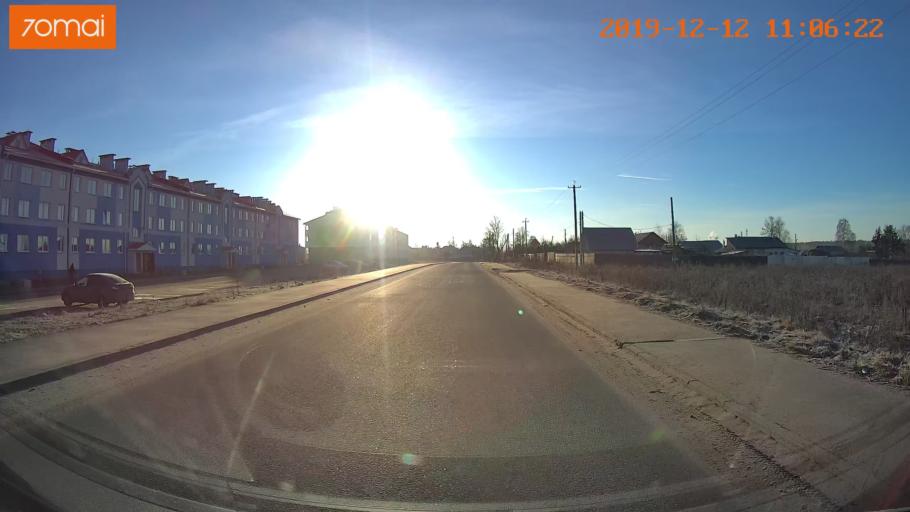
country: RU
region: Ivanovo
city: Kokhma
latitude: 56.9448
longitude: 41.0883
